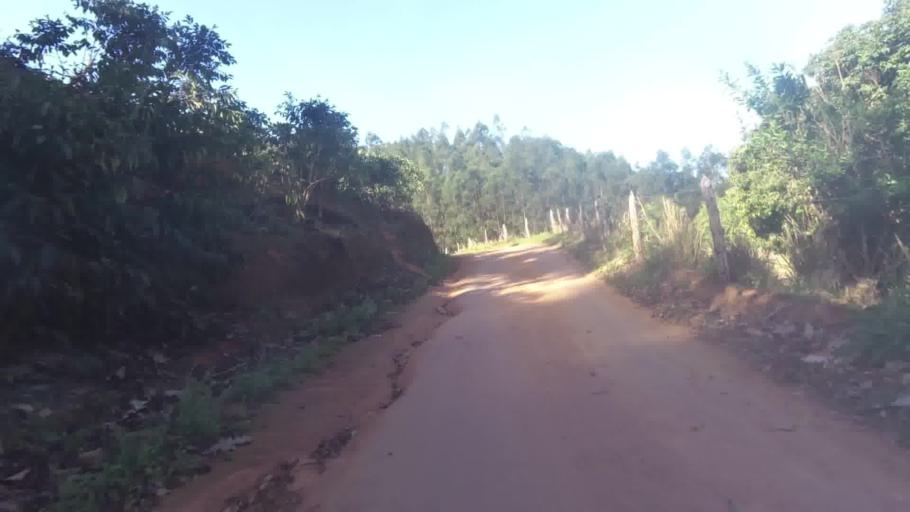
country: BR
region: Espirito Santo
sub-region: Iconha
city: Iconha
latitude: -20.7453
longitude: -40.7973
